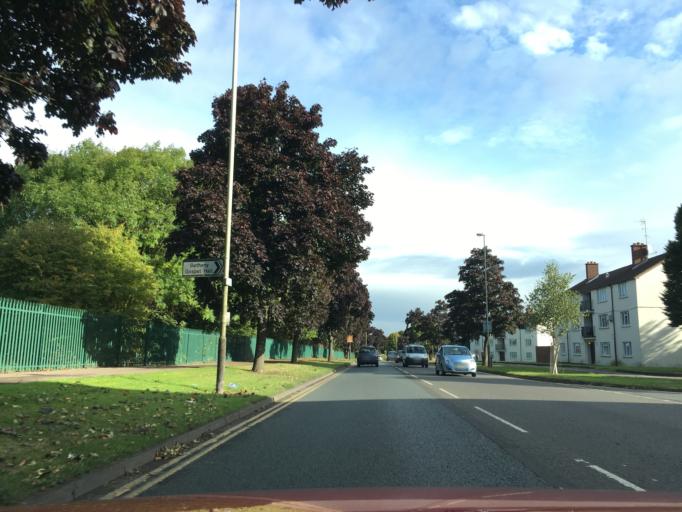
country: GB
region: England
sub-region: Gloucestershire
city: Uckington
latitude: 51.9041
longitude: -2.1148
